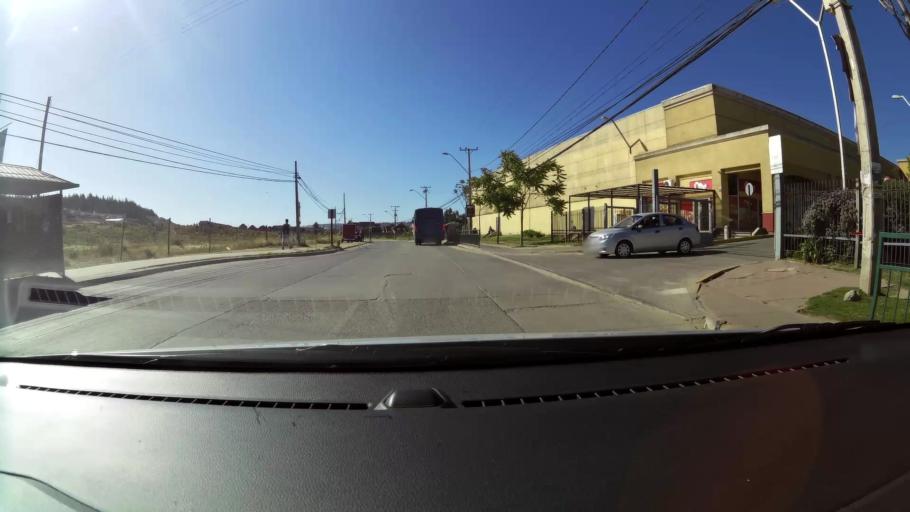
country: CL
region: Valparaiso
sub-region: Provincia de Valparaiso
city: Vina del Mar
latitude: -33.1313
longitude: -71.5655
